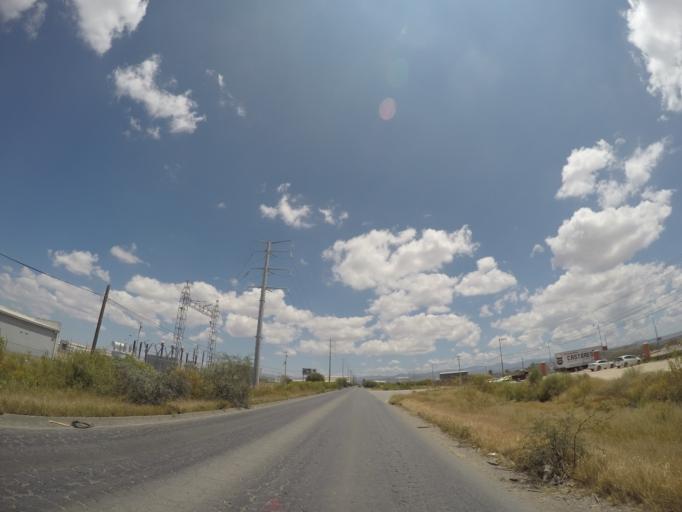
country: MX
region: San Luis Potosi
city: La Pila
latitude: 22.0449
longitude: -100.8790
